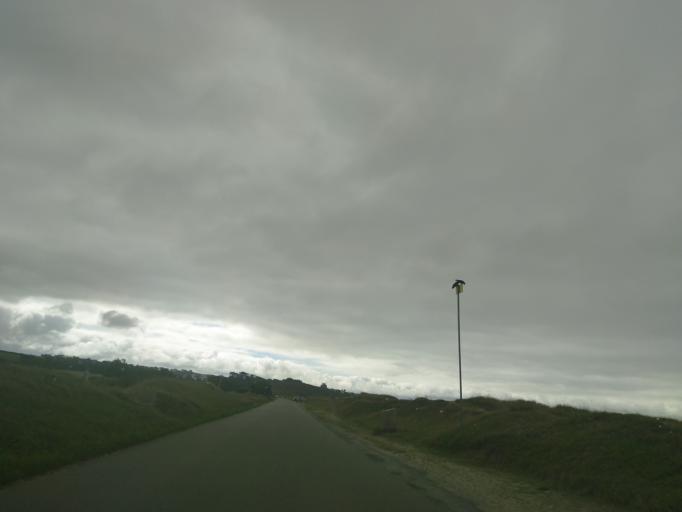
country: FR
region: Brittany
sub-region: Departement du Finistere
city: Plomodiern
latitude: 48.1821
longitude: -4.2945
